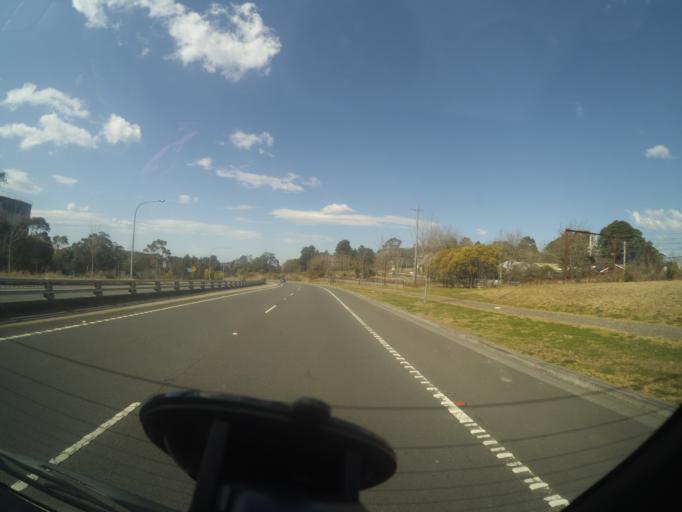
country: AU
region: New South Wales
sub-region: Blue Mountains Municipality
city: Leura
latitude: -33.7117
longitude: 150.3372
